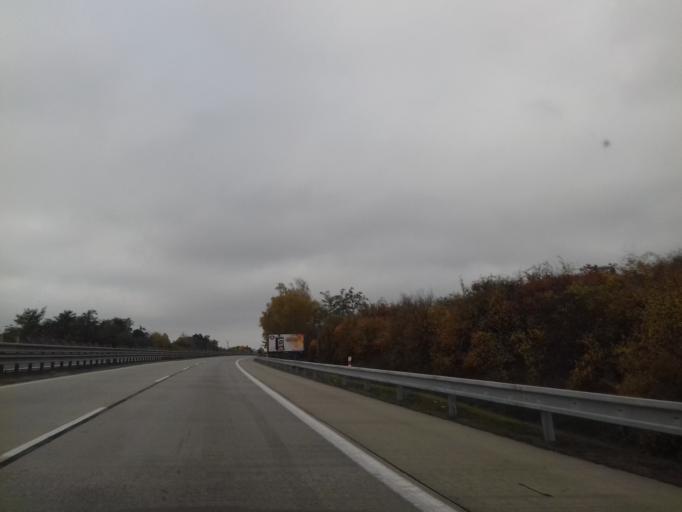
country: CZ
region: South Moravian
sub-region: Okres Breclav
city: Hustopece
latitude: 48.9364
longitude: 16.7439
